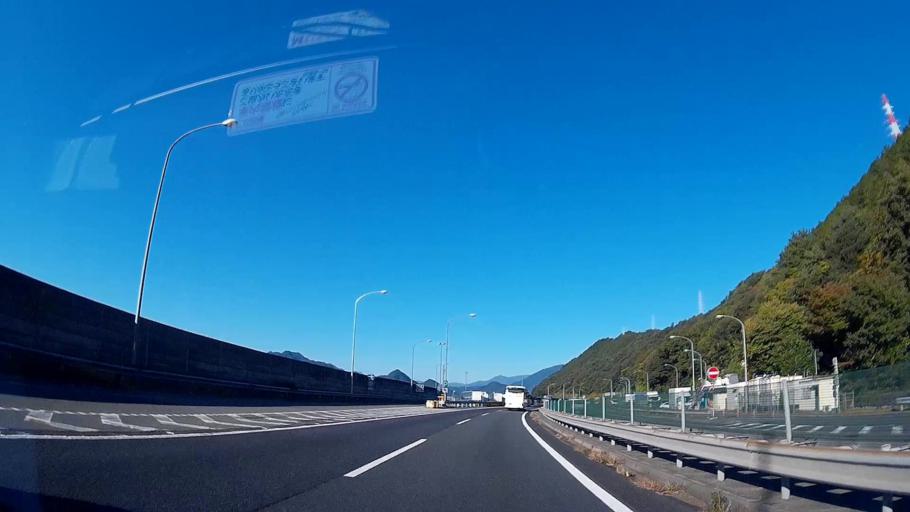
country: JP
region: Yamanashi
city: Uenohara
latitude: 35.6156
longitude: 139.1590
